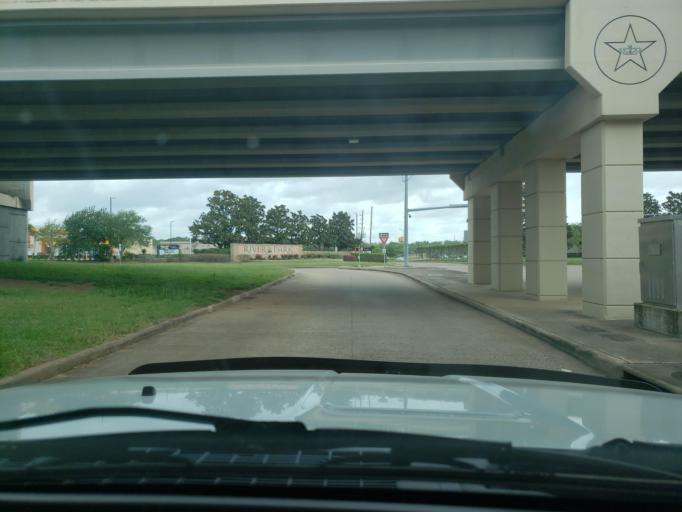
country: US
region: Texas
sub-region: Fort Bend County
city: New Territory
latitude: 29.5744
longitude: -95.6811
